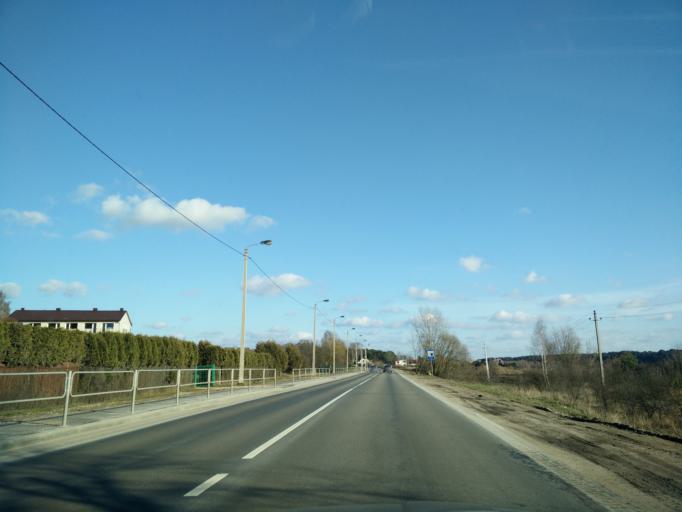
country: LT
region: Kauno apskritis
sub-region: Kauno rajonas
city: Akademija (Kaunas)
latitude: 54.9217
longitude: 23.7981
